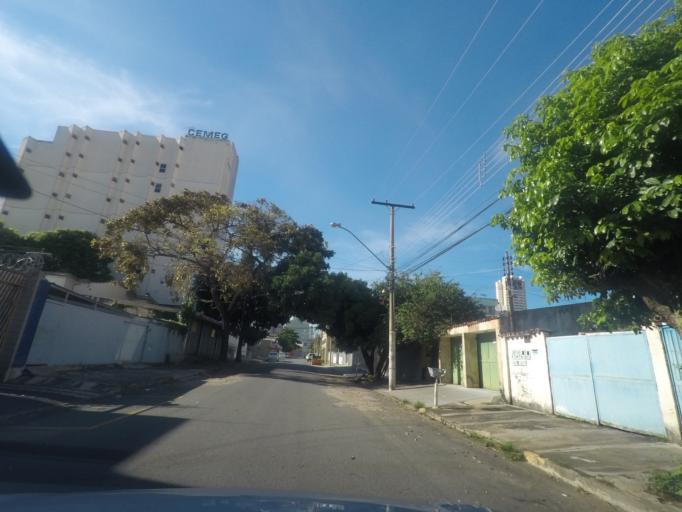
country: BR
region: Goias
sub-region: Goiania
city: Goiania
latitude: -16.6757
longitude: -49.2692
